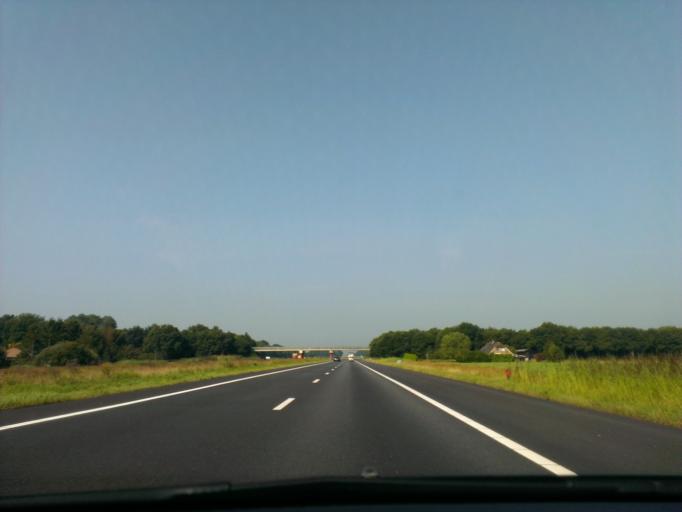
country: NL
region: Drenthe
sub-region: Gemeente Hoogeveen
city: Hoogeveen
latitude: 52.7139
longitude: 6.5771
